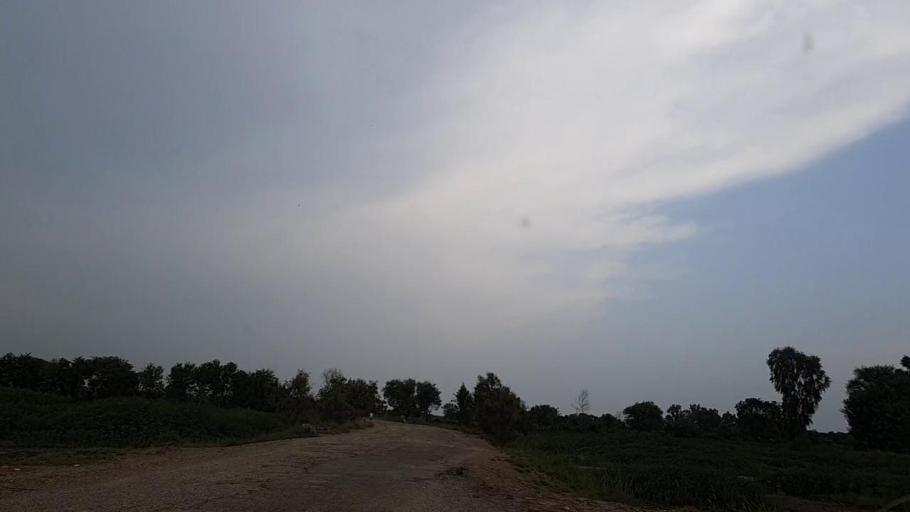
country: PK
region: Sindh
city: Mirpur Mathelo
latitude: 27.8925
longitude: 69.6507
